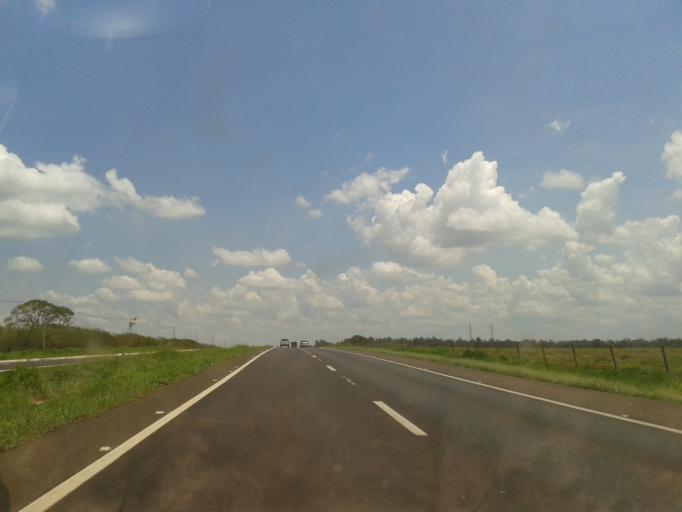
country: BR
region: Minas Gerais
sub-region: Uberlandia
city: Uberlandia
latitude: -18.8797
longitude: -48.4998
